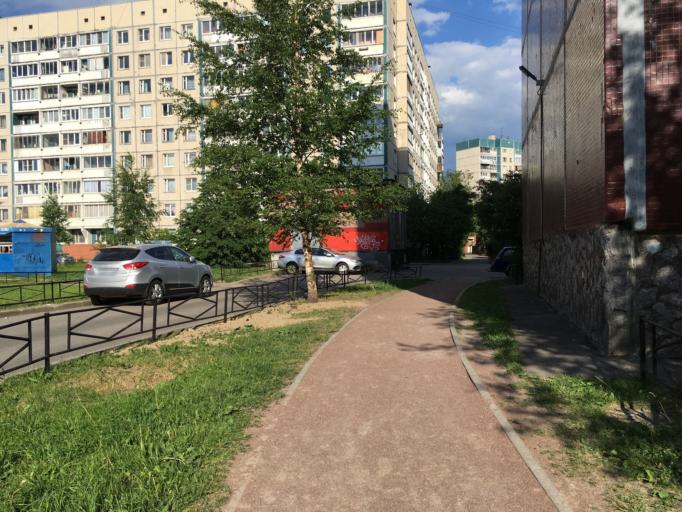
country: RU
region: St.-Petersburg
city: Komendantsky aerodrom
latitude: 60.0157
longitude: 30.2549
